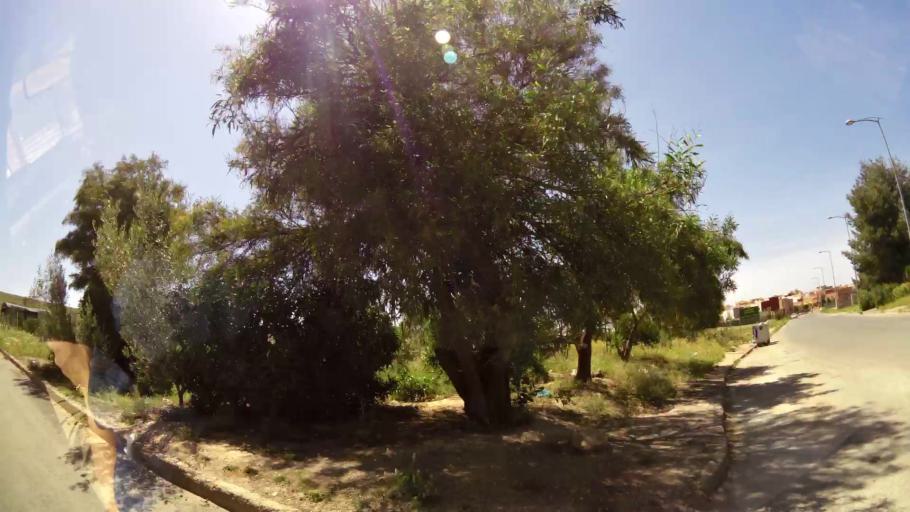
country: MA
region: Oriental
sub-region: Oujda-Angad
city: Oujda
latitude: 34.6497
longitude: -1.9121
